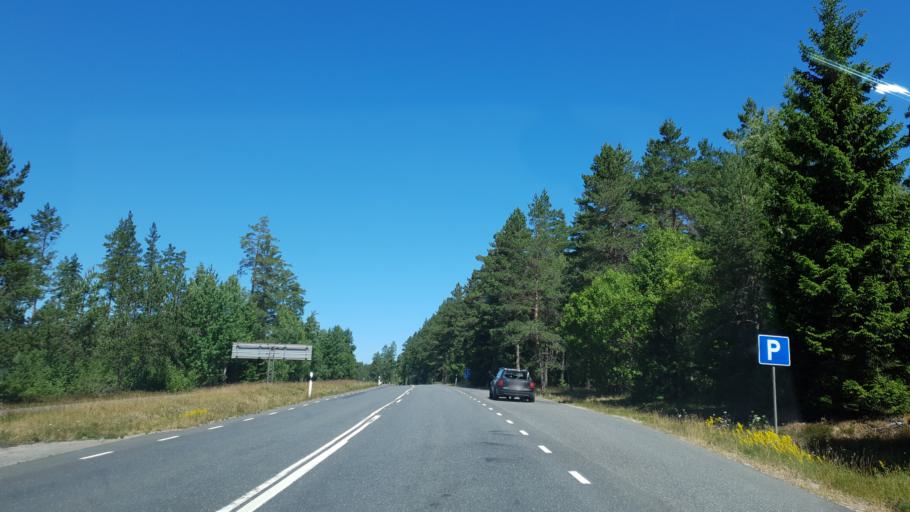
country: SE
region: Joenkoeping
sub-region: Vaggeryds Kommun
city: Vaggeryd
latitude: 57.5248
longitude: 14.1378
